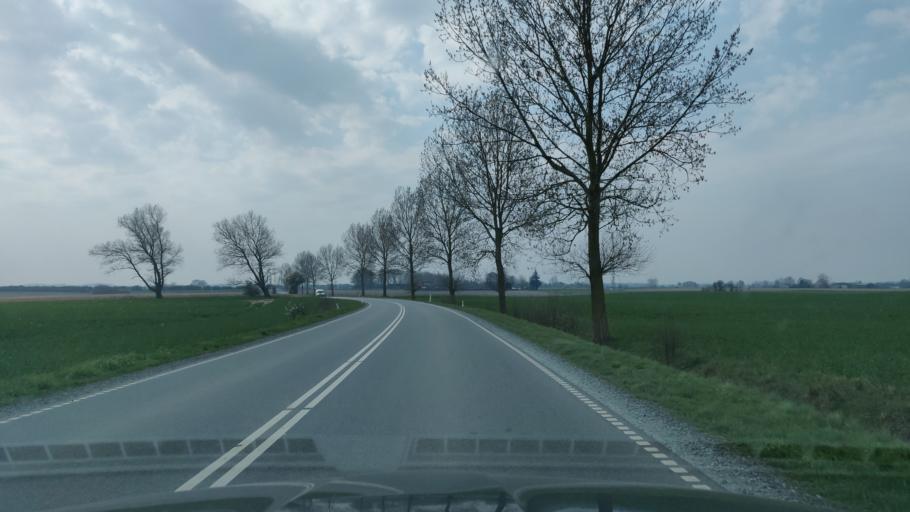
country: DK
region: South Denmark
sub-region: Nordfyns Kommune
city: Sonderso
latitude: 55.4953
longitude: 10.2407
